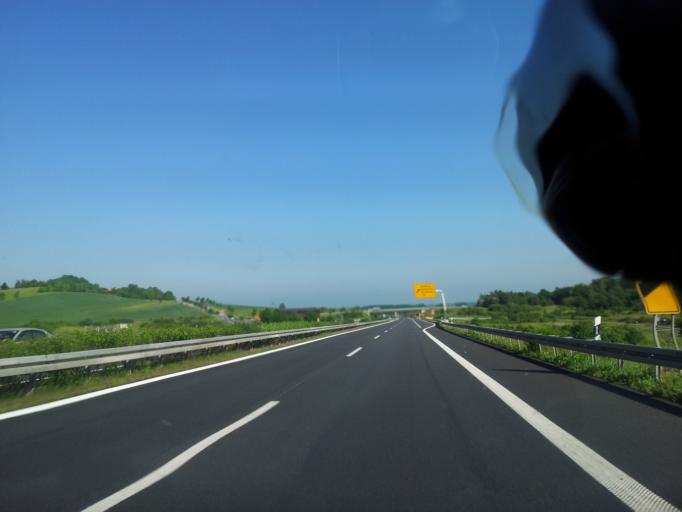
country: DE
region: Saxony-Anhalt
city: Blankenburg
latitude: 51.8223
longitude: 10.9270
